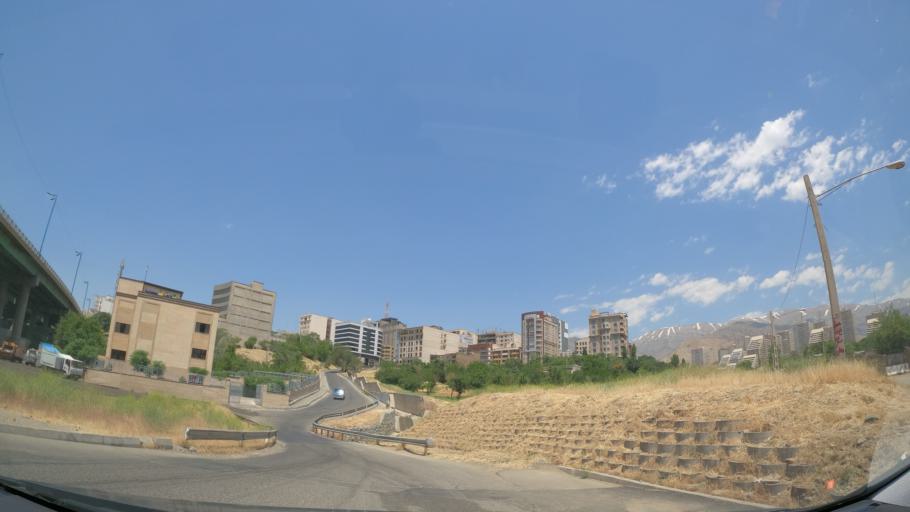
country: IR
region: Tehran
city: Tajrish
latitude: 35.7787
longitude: 51.3885
